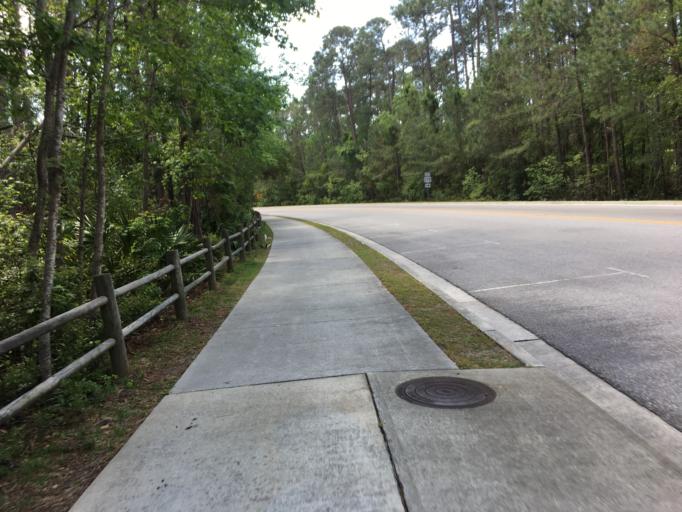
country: US
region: South Carolina
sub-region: Beaufort County
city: Hilton Head Island
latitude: 32.1716
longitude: -80.7728
